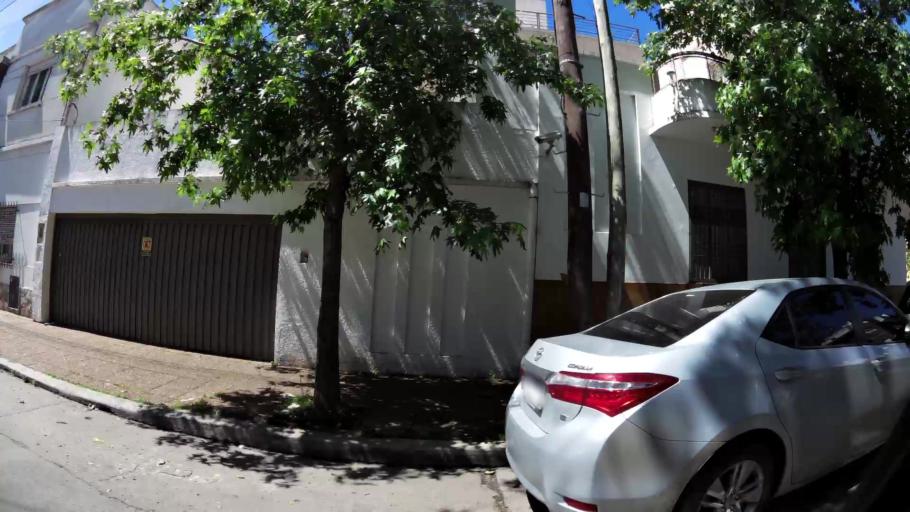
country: AR
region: Buenos Aires
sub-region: Partido de Quilmes
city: Quilmes
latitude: -34.7269
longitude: -58.2498
